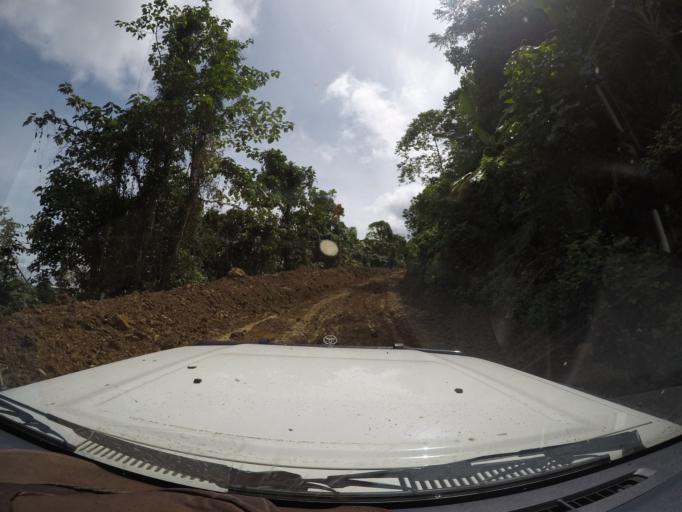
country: PG
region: Gulf
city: Kerema
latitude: -7.9922
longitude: 145.8310
